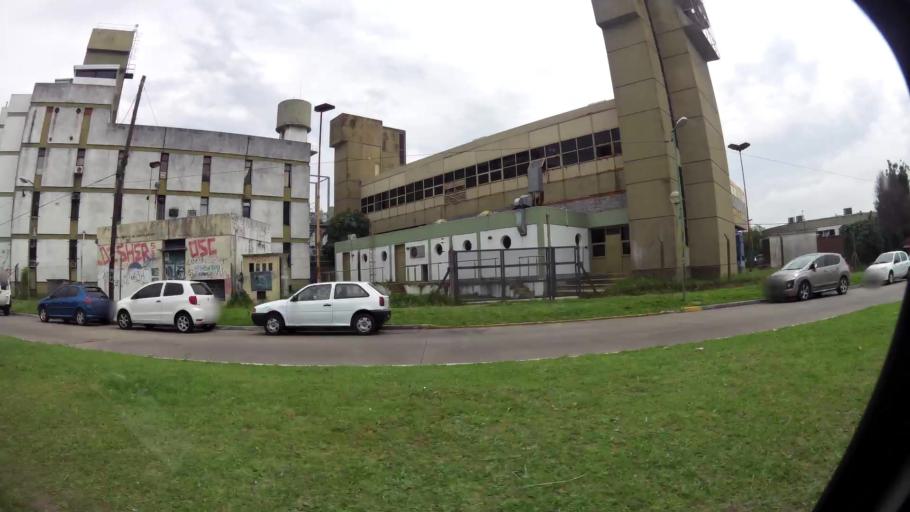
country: AR
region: Buenos Aires
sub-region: Partido de La Plata
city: La Plata
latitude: -34.8985
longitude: -57.9789
